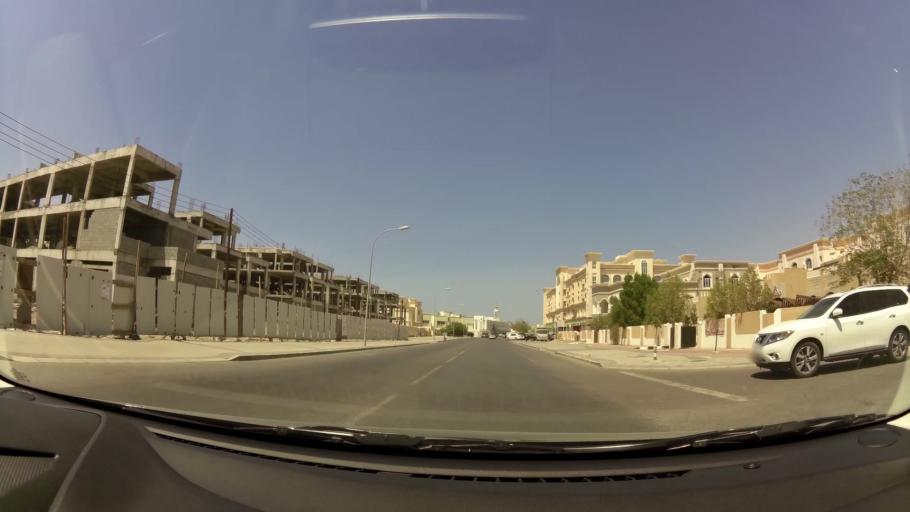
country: OM
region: Muhafazat Masqat
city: As Sib al Jadidah
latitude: 23.6309
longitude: 58.2263
